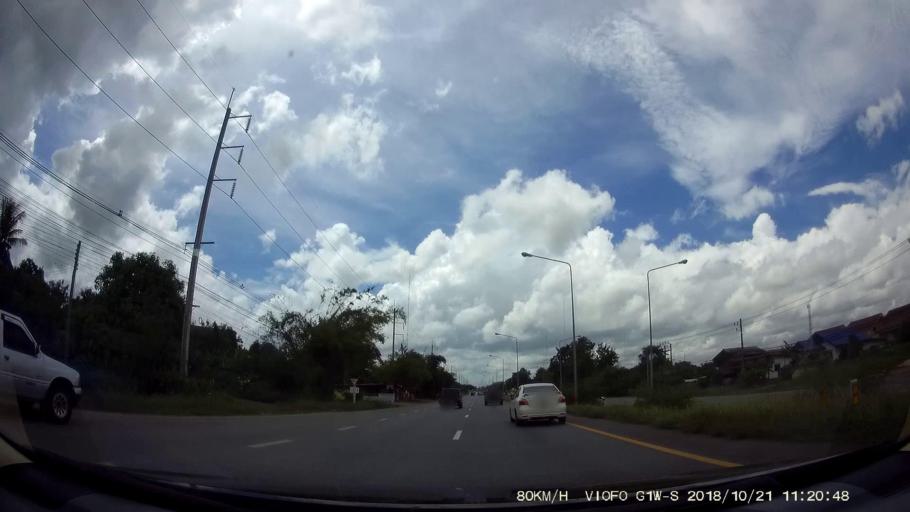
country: TH
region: Chaiyaphum
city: Chaiyaphum
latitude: 15.8532
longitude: 102.0714
